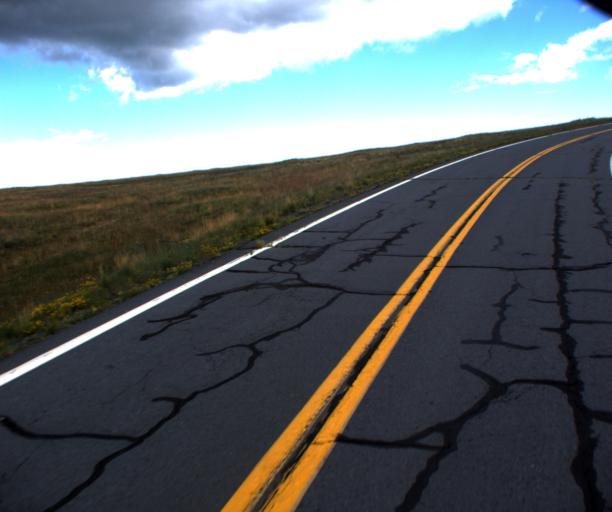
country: US
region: Arizona
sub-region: Apache County
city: Eagar
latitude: 33.9592
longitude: -109.3941
